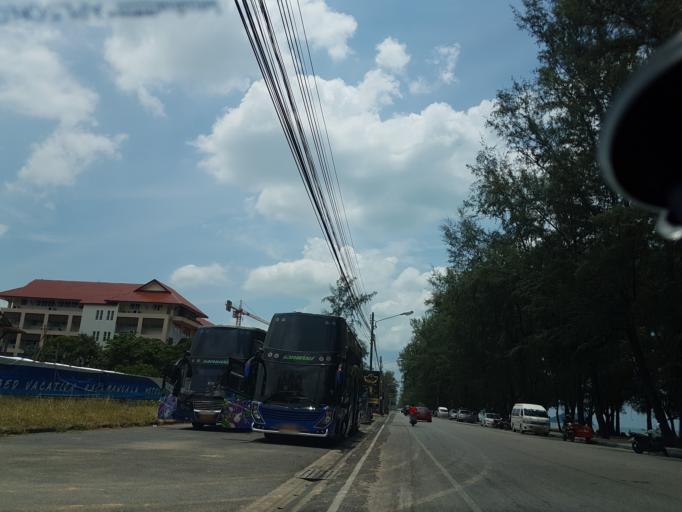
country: TH
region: Songkhla
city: Songkhla
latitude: 7.1994
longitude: 100.6050
